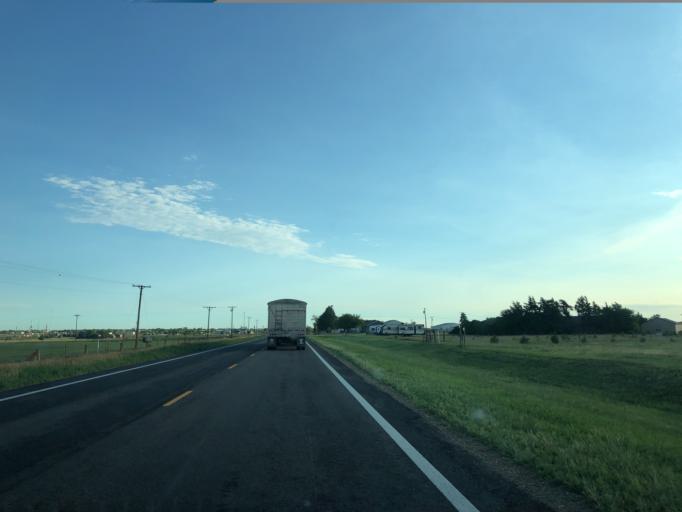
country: US
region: Kansas
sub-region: Russell County
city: Russell
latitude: 38.8544
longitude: -98.8546
